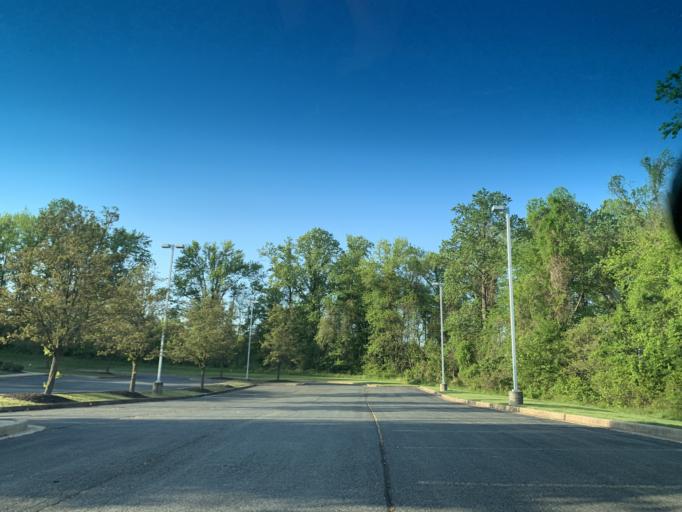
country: US
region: Maryland
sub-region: Harford County
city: Aberdeen
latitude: 39.5281
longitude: -76.1965
